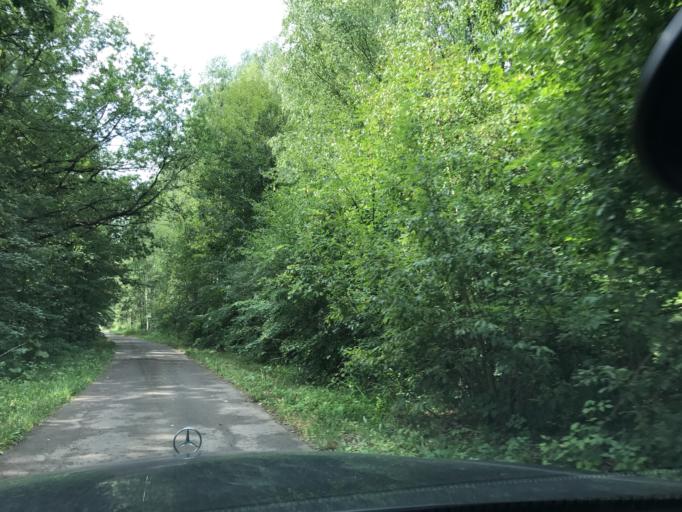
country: RU
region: Nizjnij Novgorod
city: Vacha
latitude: 55.9741
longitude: 42.7514
